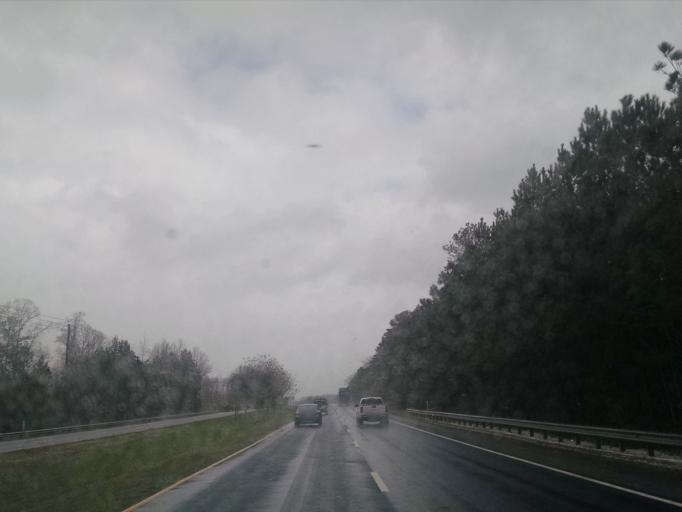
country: US
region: Georgia
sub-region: Gwinnett County
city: Sugar Hill
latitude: 34.0867
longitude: -84.0483
